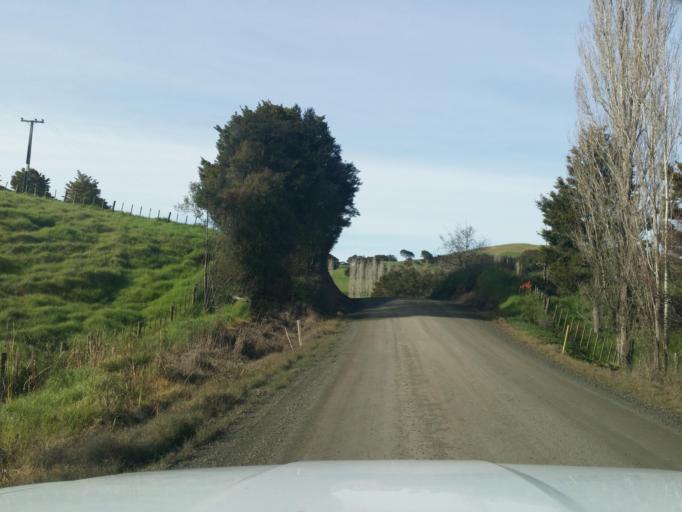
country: NZ
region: Northland
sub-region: Kaipara District
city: Dargaville
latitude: -35.8193
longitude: 173.9086
